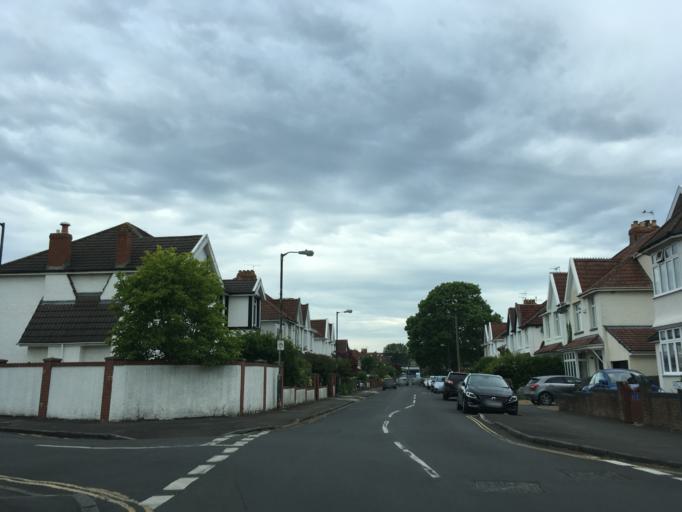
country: GB
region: England
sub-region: Bristol
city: Bristol
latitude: 51.4840
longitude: -2.6078
